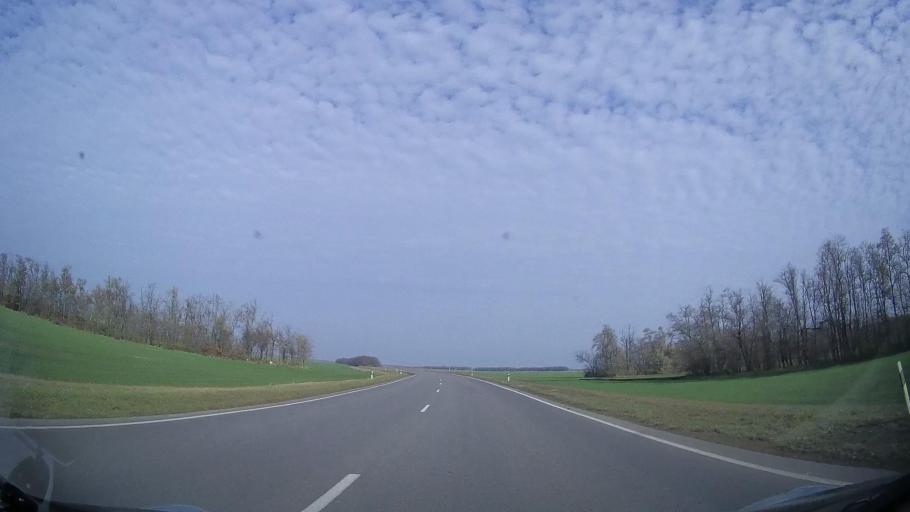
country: RU
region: Rostov
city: Tselina
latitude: 46.5162
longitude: 41.0717
